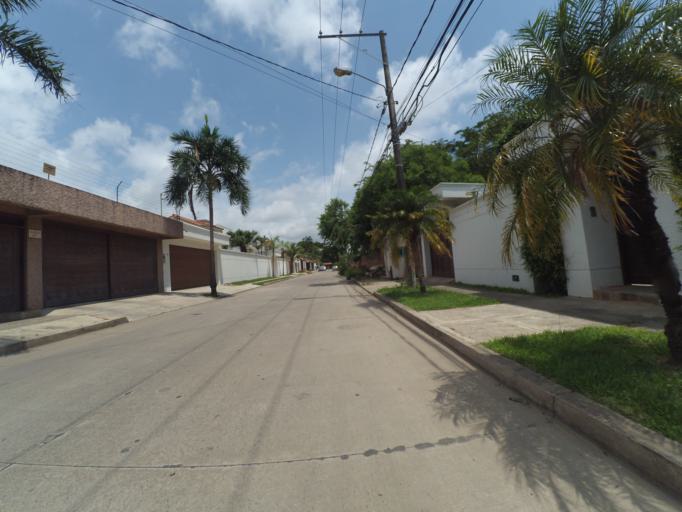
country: BO
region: Santa Cruz
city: Santa Cruz de la Sierra
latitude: -17.8024
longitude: -63.2133
